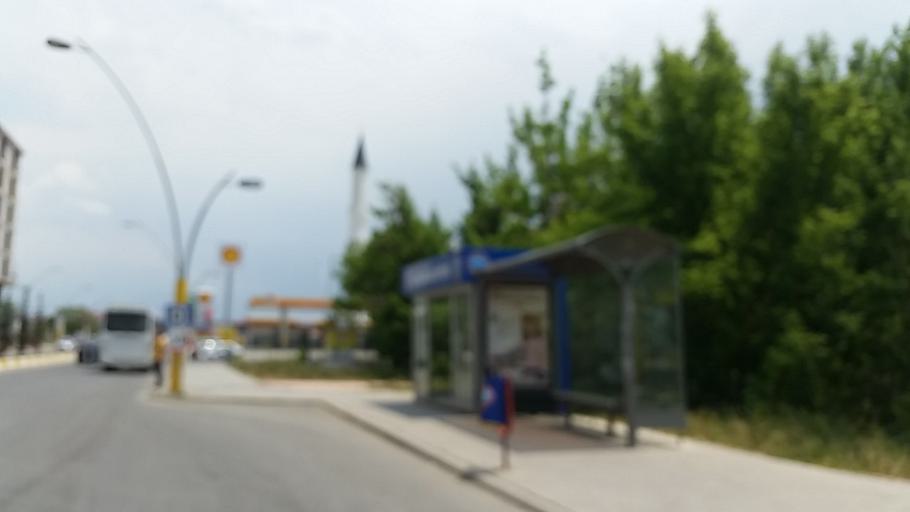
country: TR
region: Agri
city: Agri
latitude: 39.7189
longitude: 43.0325
